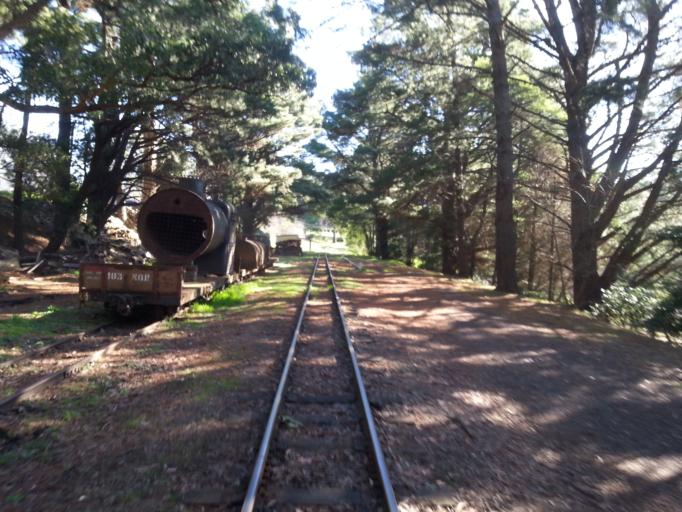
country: AU
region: Victoria
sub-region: Cardinia
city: Emerald
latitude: -37.9287
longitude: 145.4244
